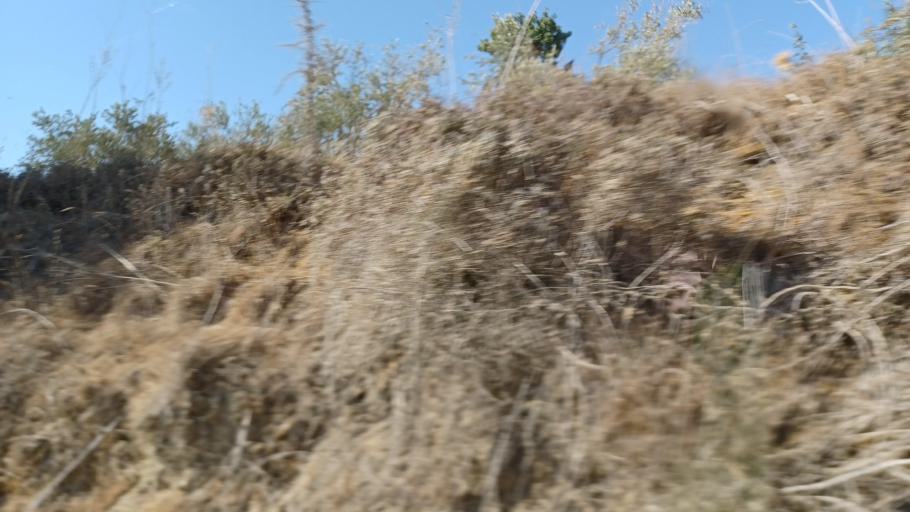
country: CY
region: Pafos
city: Tala
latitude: 34.9299
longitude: 32.4859
